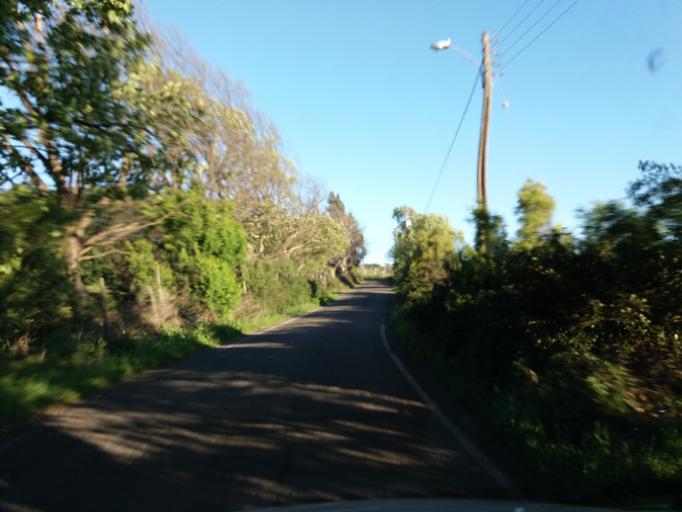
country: CL
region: Valparaiso
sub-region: Provincia de Quillota
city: Quillota
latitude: -32.9142
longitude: -71.3371
